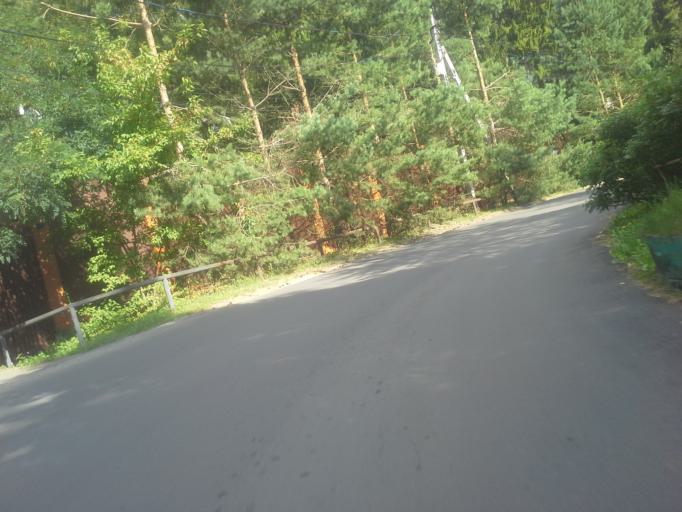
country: RU
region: Moskovskaya
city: Selyatino
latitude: 55.4744
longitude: 37.0119
